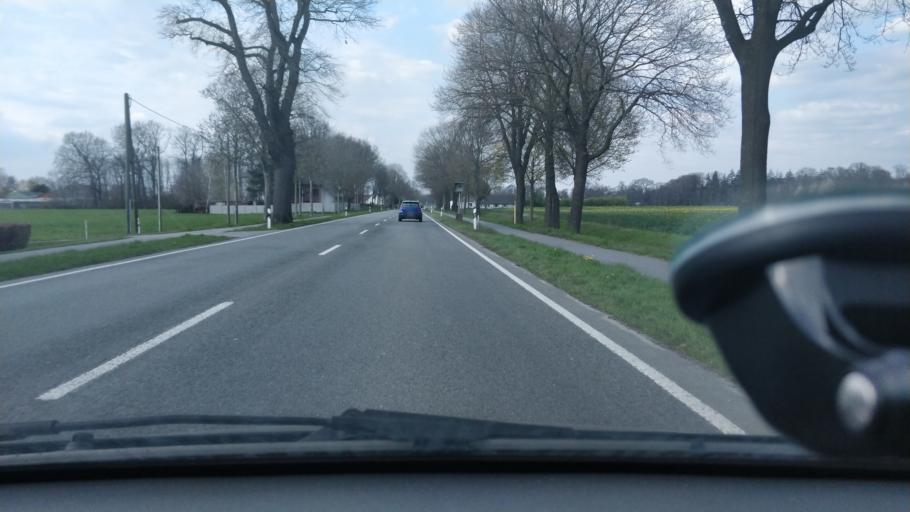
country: DE
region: North Rhine-Westphalia
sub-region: Regierungsbezirk Dusseldorf
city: Hamminkeln
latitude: 51.7037
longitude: 6.6019
